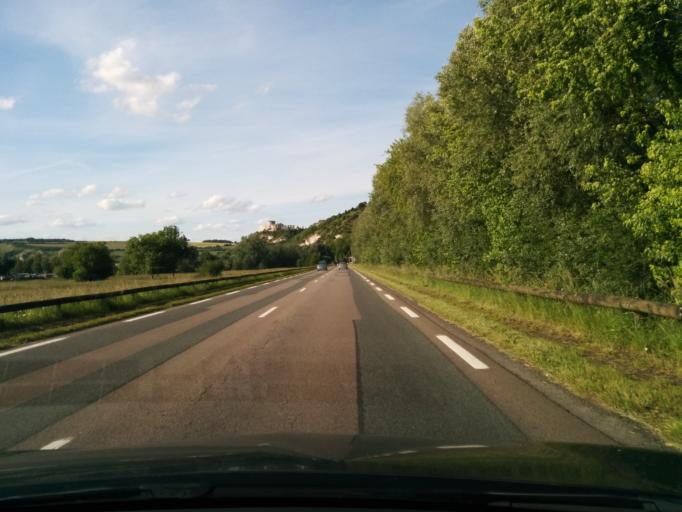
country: FR
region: Haute-Normandie
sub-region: Departement de l'Eure
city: Les Andelys
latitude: 49.2269
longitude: 1.3982
